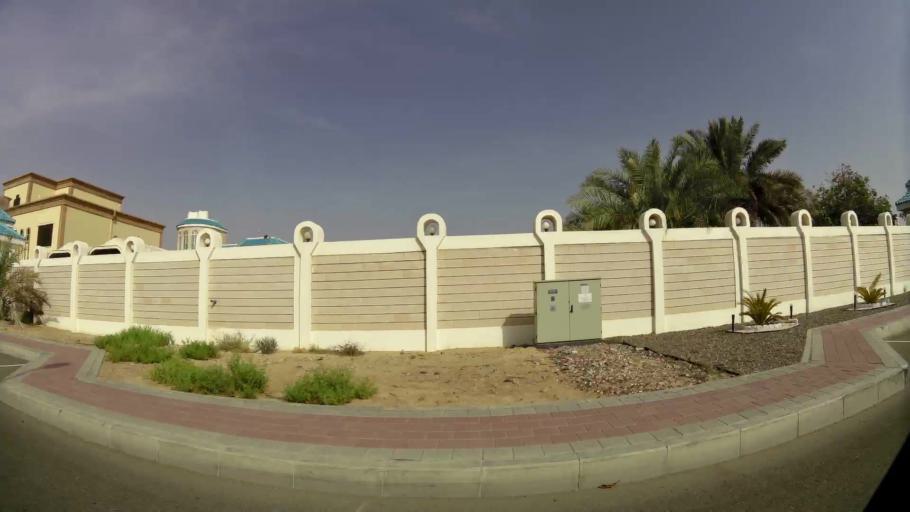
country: AE
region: Abu Dhabi
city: Al Ain
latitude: 24.1353
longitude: 55.7042
